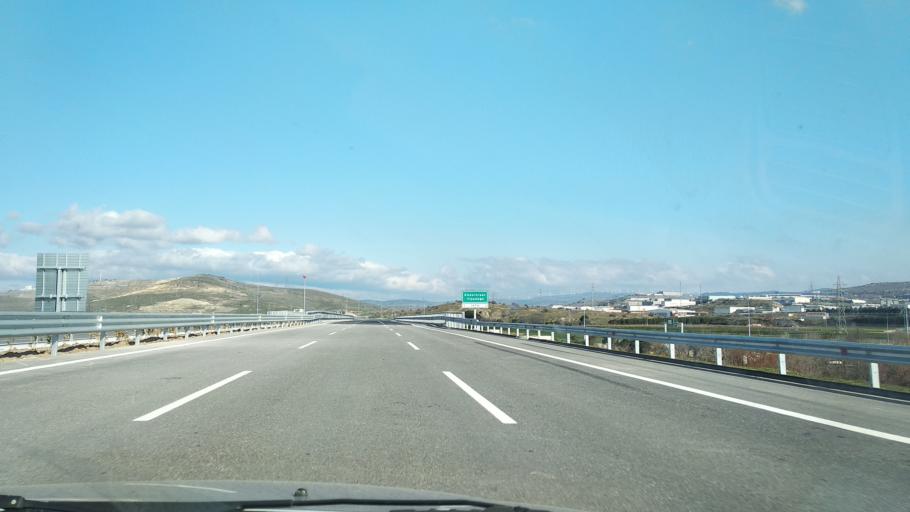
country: TR
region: Izmir
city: Aliaga
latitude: 38.8112
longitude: 27.0226
